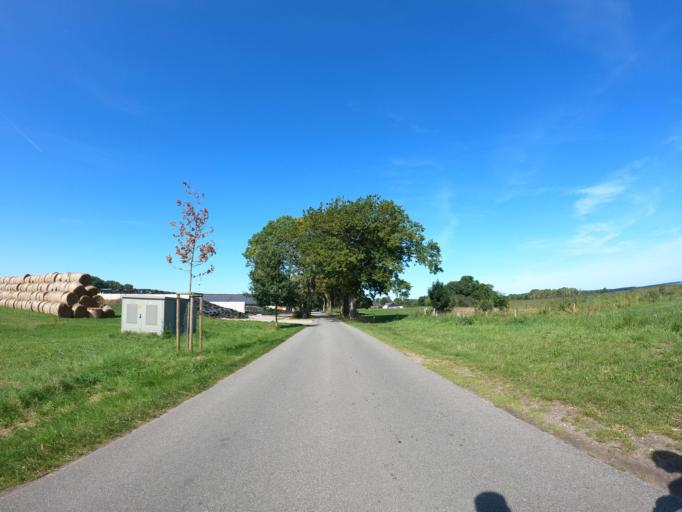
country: DE
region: Mecklenburg-Vorpommern
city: Prohn
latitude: 54.4008
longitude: 13.0203
